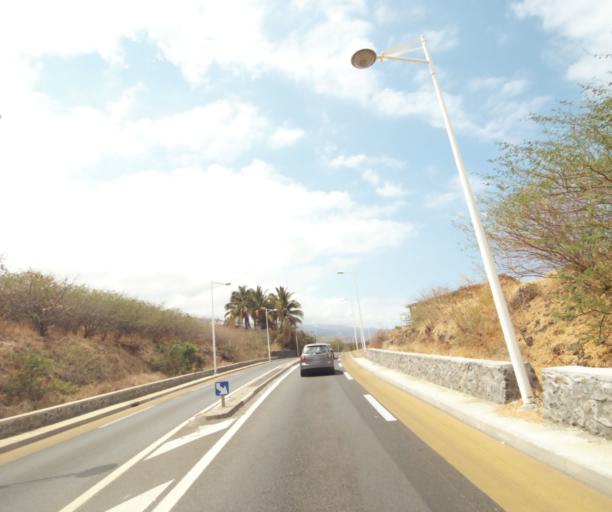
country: RE
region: Reunion
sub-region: Reunion
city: Trois-Bassins
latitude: -21.0980
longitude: 55.2475
